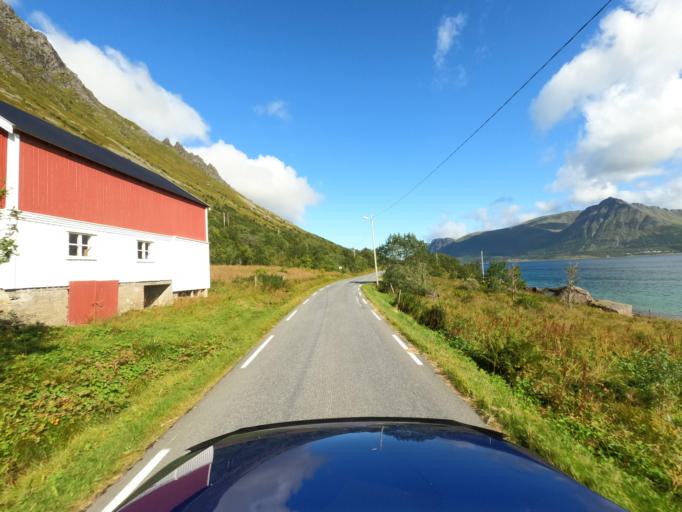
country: NO
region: Nordland
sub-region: Vagan
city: Kabelvag
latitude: 68.2730
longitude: 14.2516
